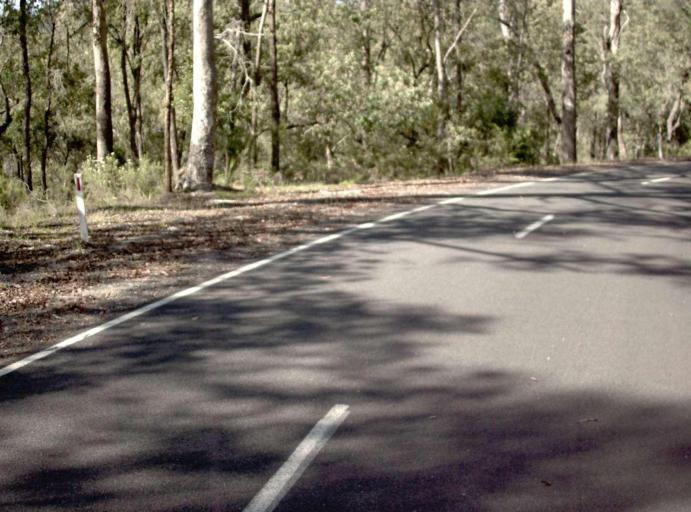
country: AU
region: New South Wales
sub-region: Bombala
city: Bombala
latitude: -37.3792
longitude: 148.6619
